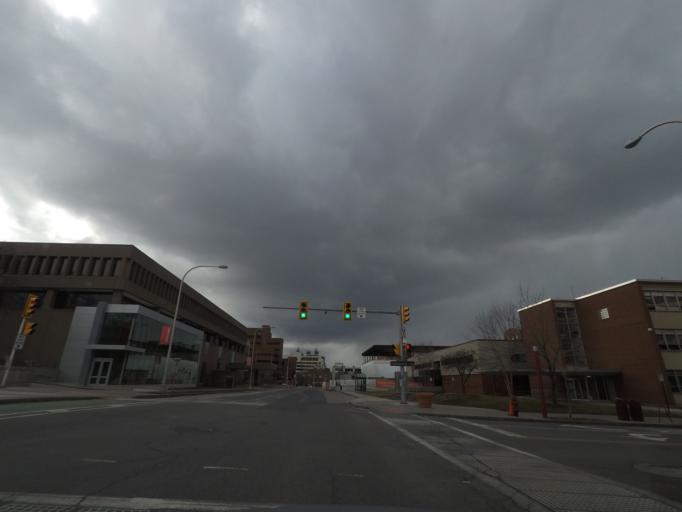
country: US
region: New York
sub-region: Onondaga County
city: Syracuse
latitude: 43.0406
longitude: -76.1343
